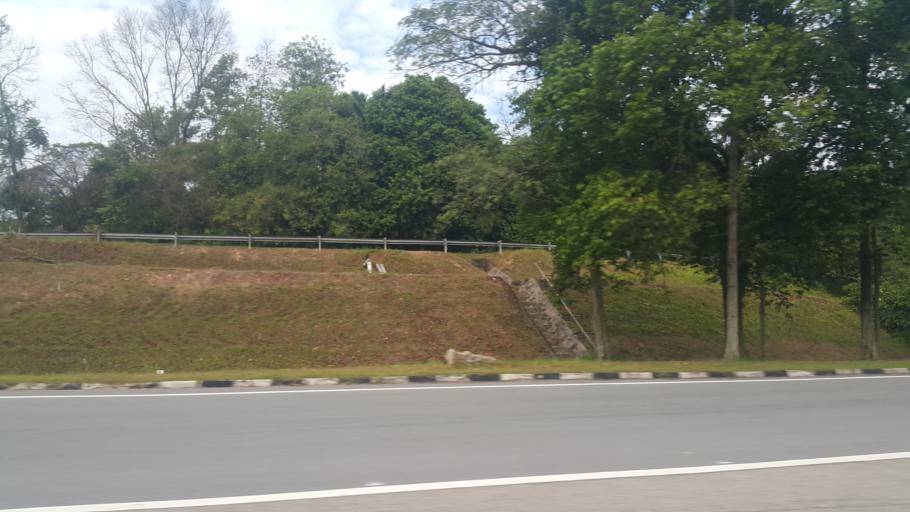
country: MY
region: Johor
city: Pekan Nenas
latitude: 1.3954
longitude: 103.5875
